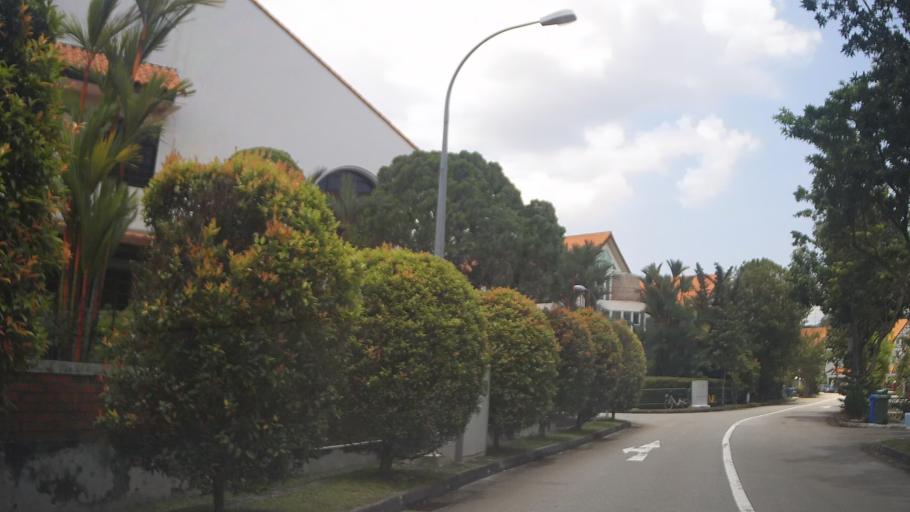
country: MY
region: Johor
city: Kampung Pasir Gudang Baru
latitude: 1.3895
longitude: 103.8560
